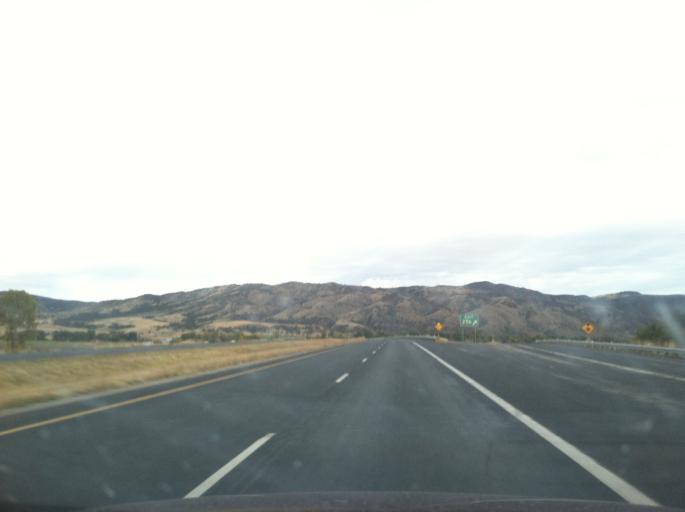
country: US
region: Montana
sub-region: Jefferson County
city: Whitehall
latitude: 45.8702
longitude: -111.9590
